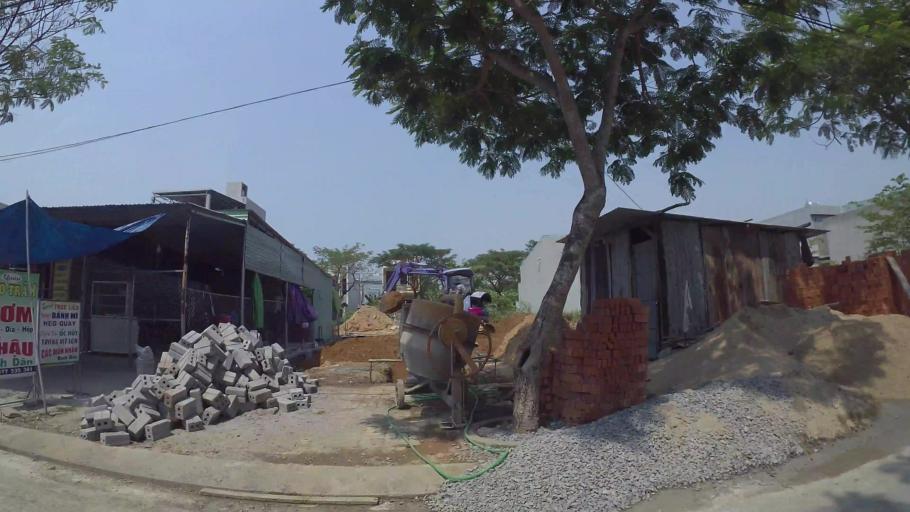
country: VN
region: Da Nang
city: Cam Le
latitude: 15.9956
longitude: 108.1974
